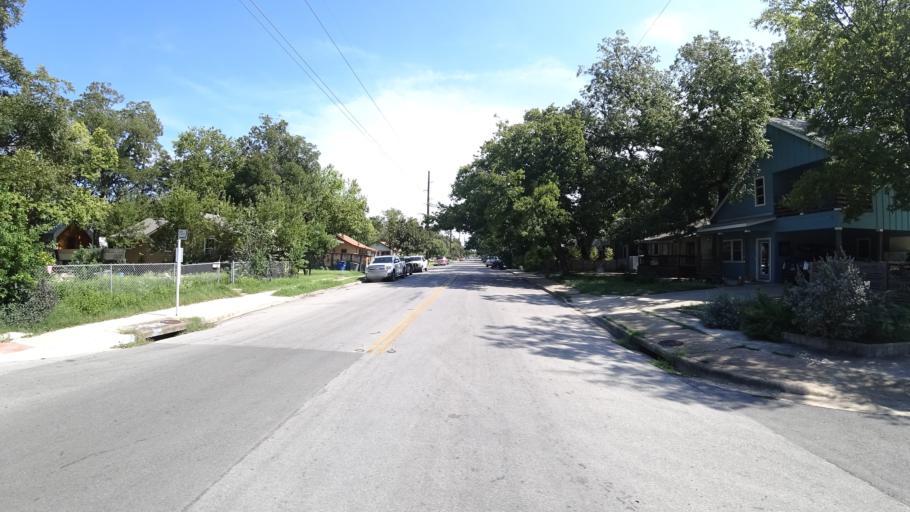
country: US
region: Texas
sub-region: Travis County
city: Austin
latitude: 30.2530
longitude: -97.7250
